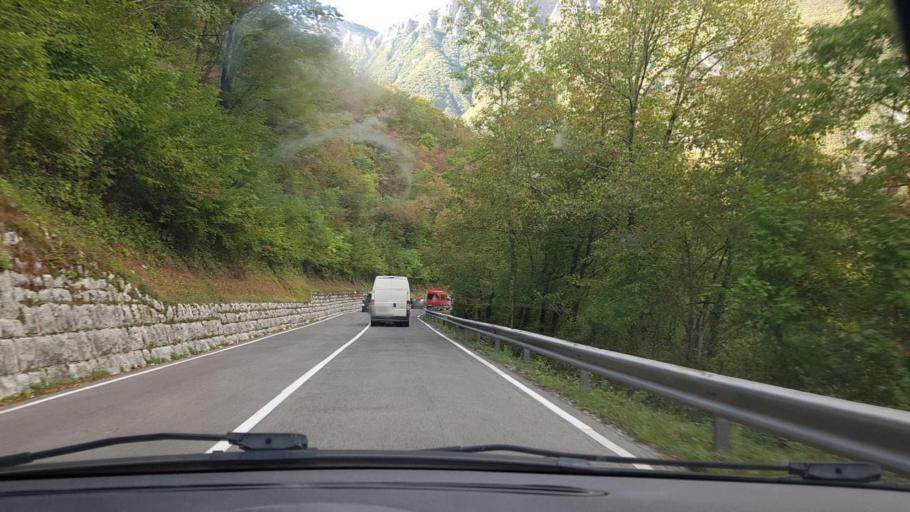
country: SI
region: Kobarid
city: Kobarid
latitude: 46.2708
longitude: 13.5706
